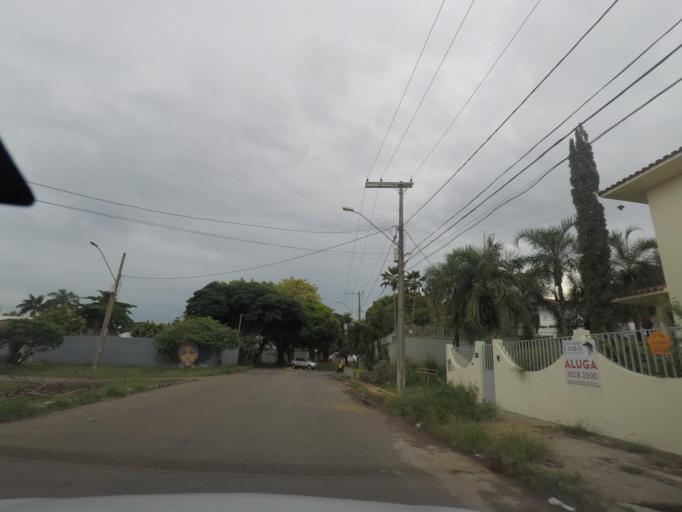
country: BR
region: Goias
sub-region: Goiania
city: Goiania
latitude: -16.6948
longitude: -49.2482
